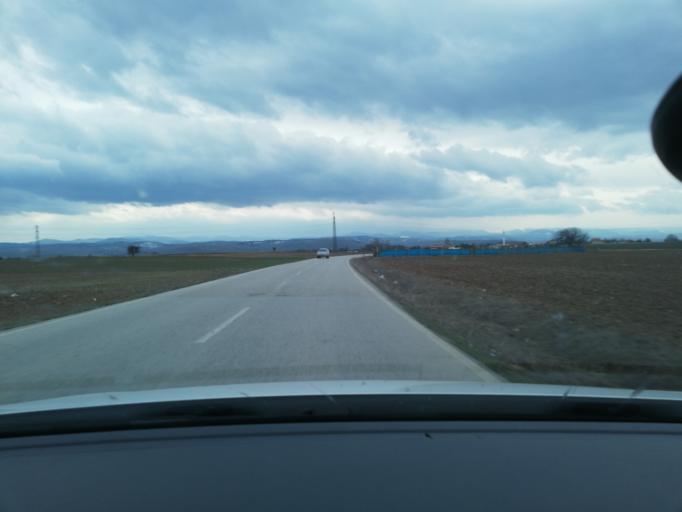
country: TR
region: Bolu
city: Gerede
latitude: 40.7662
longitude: 32.2008
